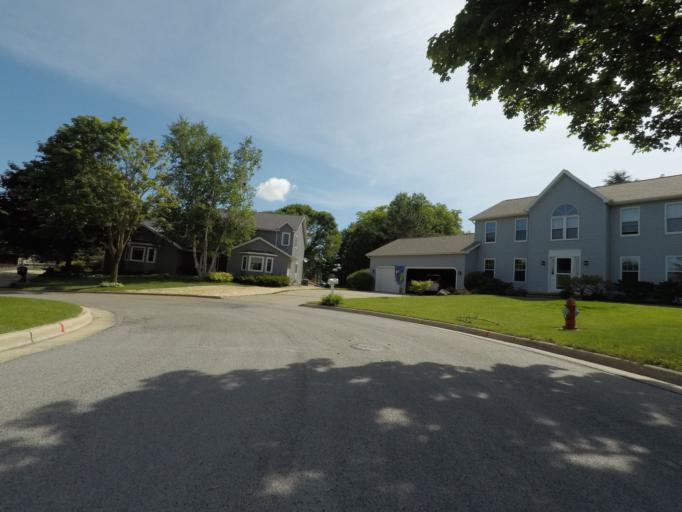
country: US
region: Wisconsin
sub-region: Dane County
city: Middleton
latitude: 43.0815
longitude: -89.5132
